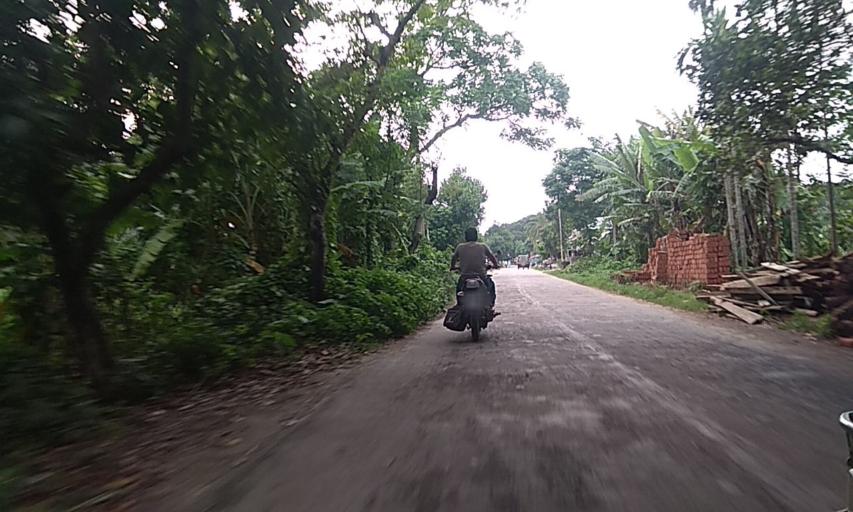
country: BD
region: Dhaka
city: Dohar
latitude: 23.4613
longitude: 89.9966
